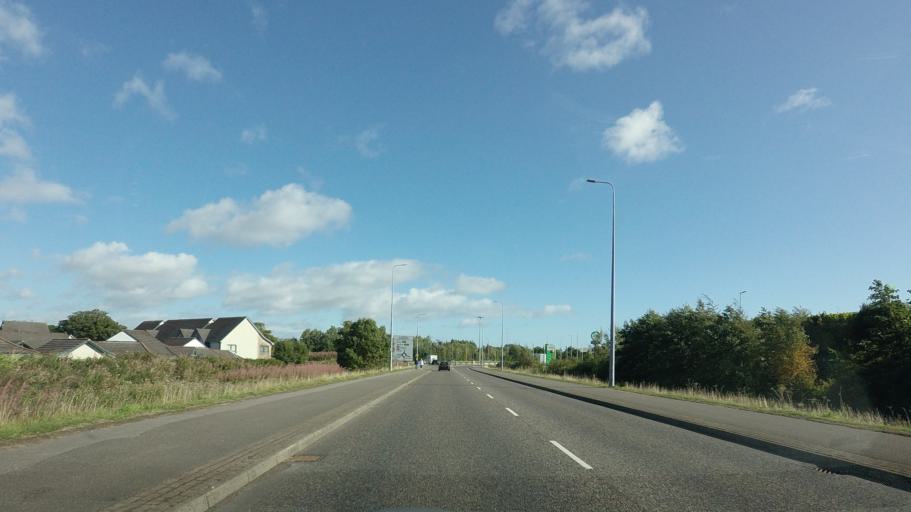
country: GB
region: Scotland
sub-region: Highland
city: Inverness
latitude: 57.4514
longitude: -4.2174
